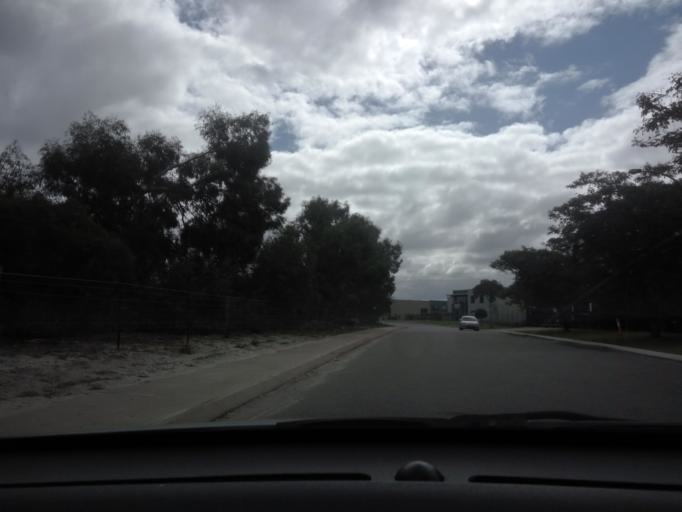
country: AU
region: Western Australia
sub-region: City of Cockburn
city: Success
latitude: -32.1235
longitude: 115.8714
